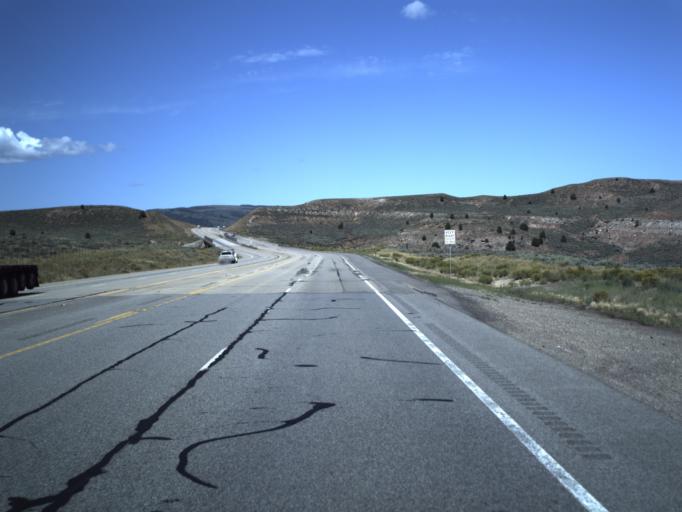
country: US
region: Utah
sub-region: Carbon County
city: Helper
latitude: 39.8420
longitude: -110.9908
